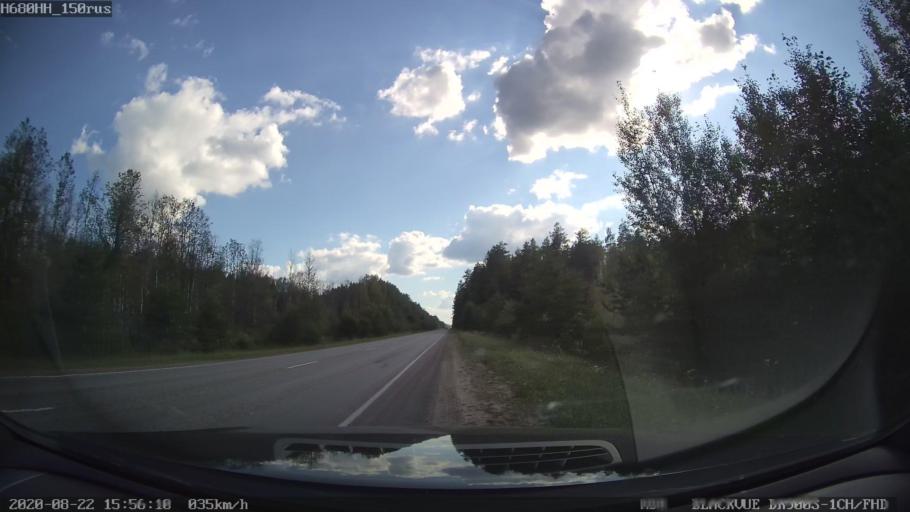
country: RU
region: Tverskaya
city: Bezhetsk
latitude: 57.6121
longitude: 36.3650
